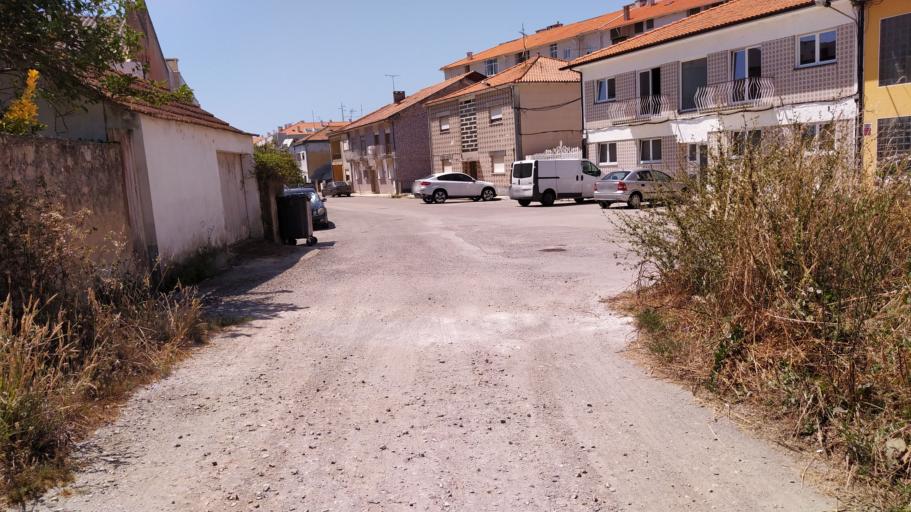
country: PT
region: Aveiro
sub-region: Aveiro
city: Aveiro
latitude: 40.6476
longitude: -8.6357
